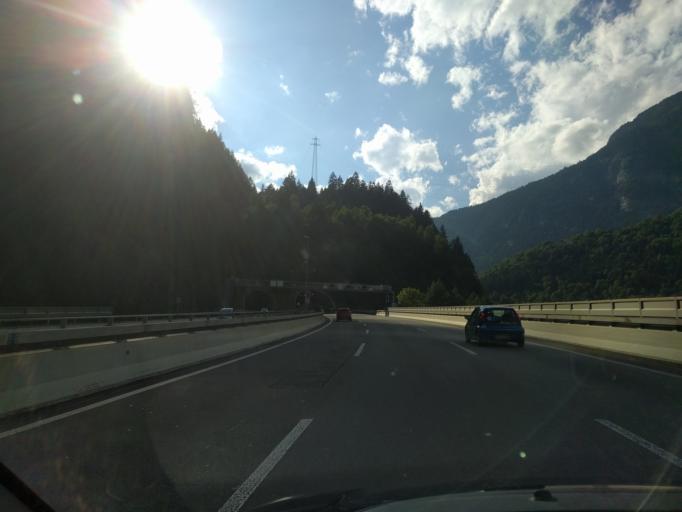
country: CH
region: Ticino
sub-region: Leventina District
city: Faido
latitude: 46.4870
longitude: 8.7747
